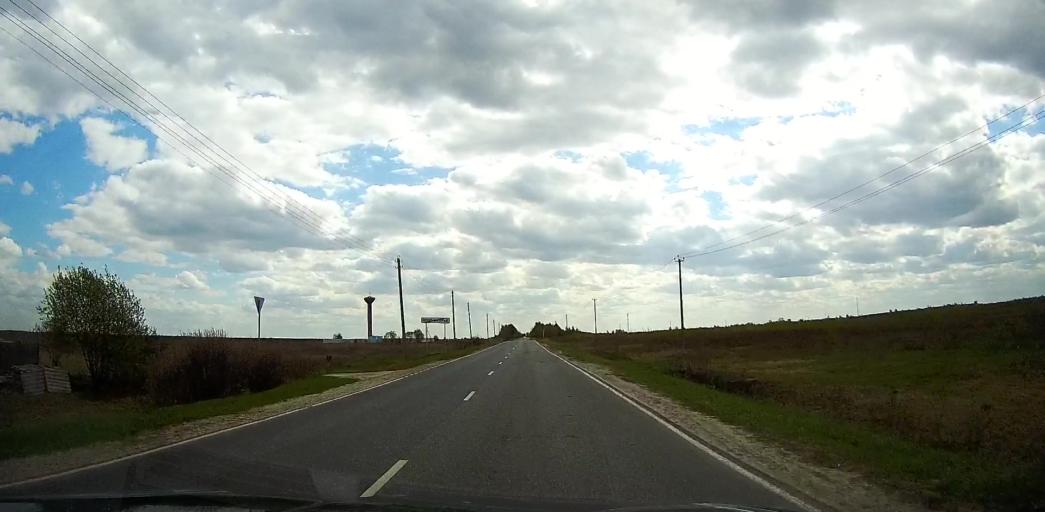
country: RU
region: Moskovskaya
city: Davydovo
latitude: 55.6417
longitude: 38.7494
